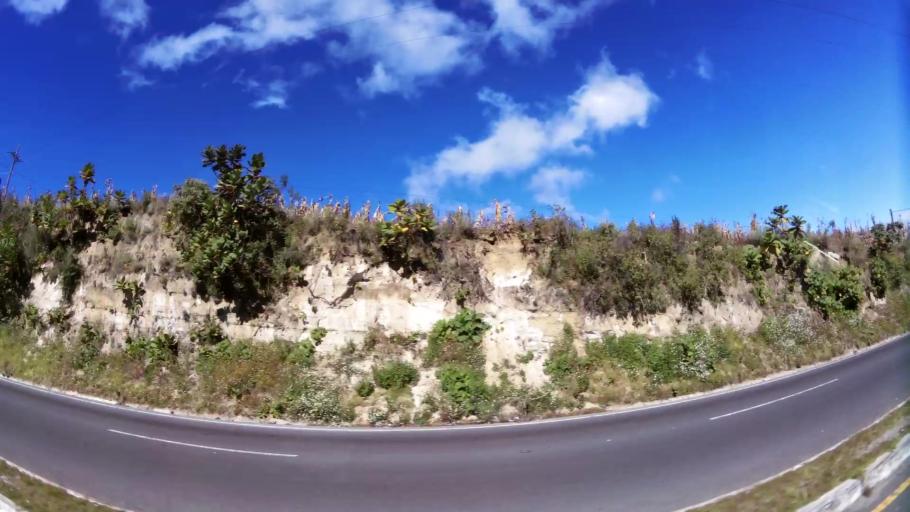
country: GT
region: Solola
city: Nahuala
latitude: 14.8243
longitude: -91.3350
